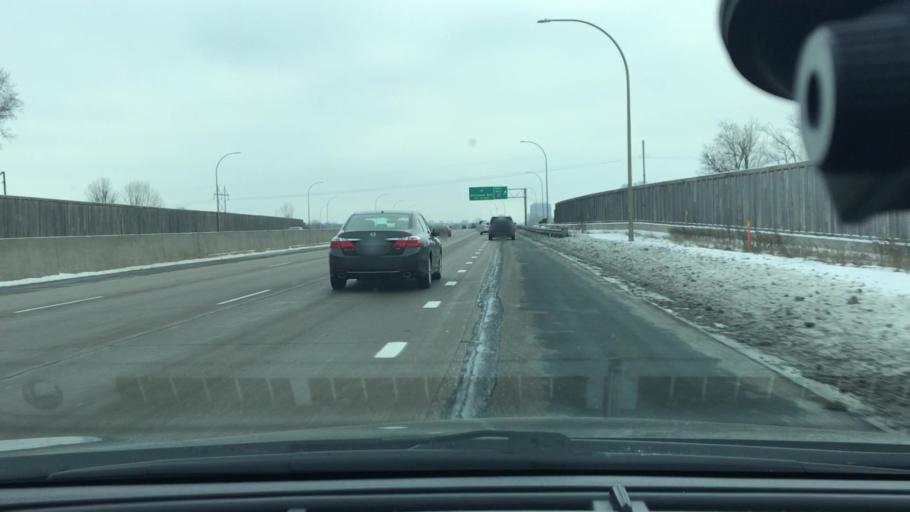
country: US
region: Minnesota
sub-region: Hennepin County
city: Golden Valley
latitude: 44.9899
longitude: -93.3497
